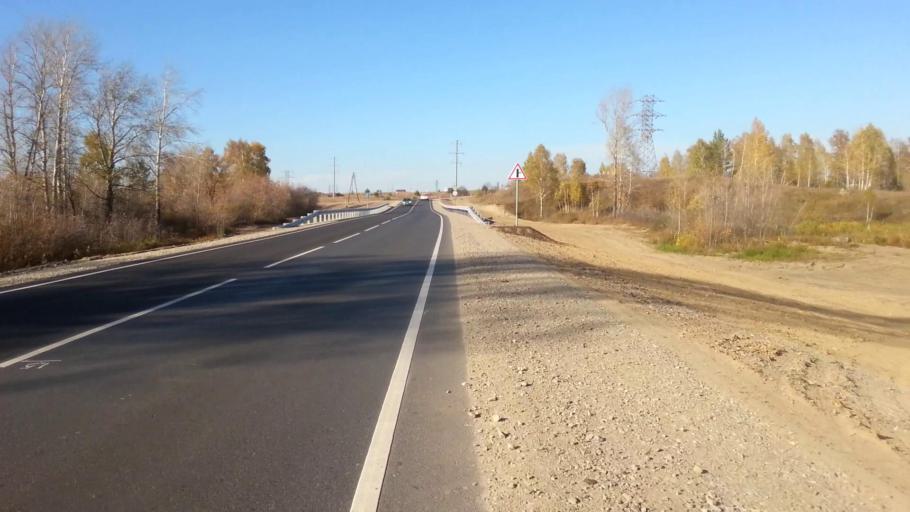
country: RU
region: Altai Krai
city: Sannikovo
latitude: 53.3263
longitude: 83.9419
